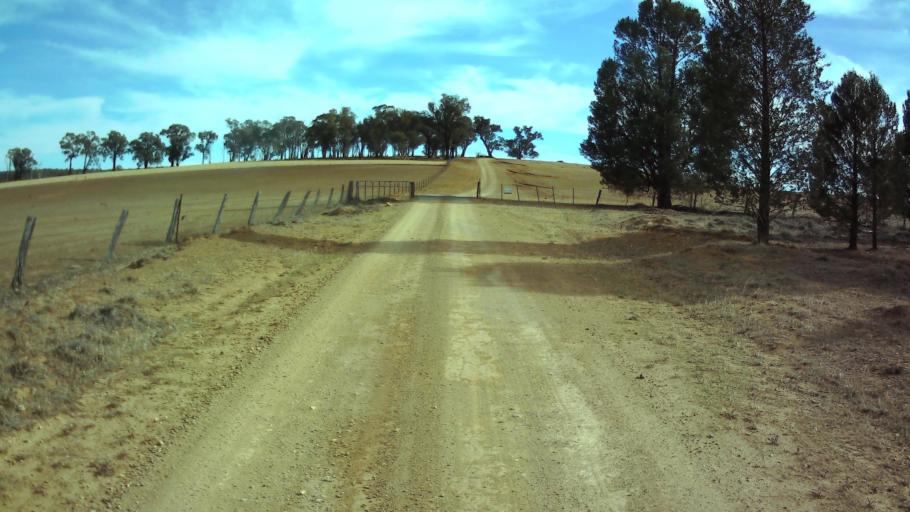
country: AU
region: New South Wales
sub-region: Weddin
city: Grenfell
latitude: -33.8967
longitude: 148.2037
